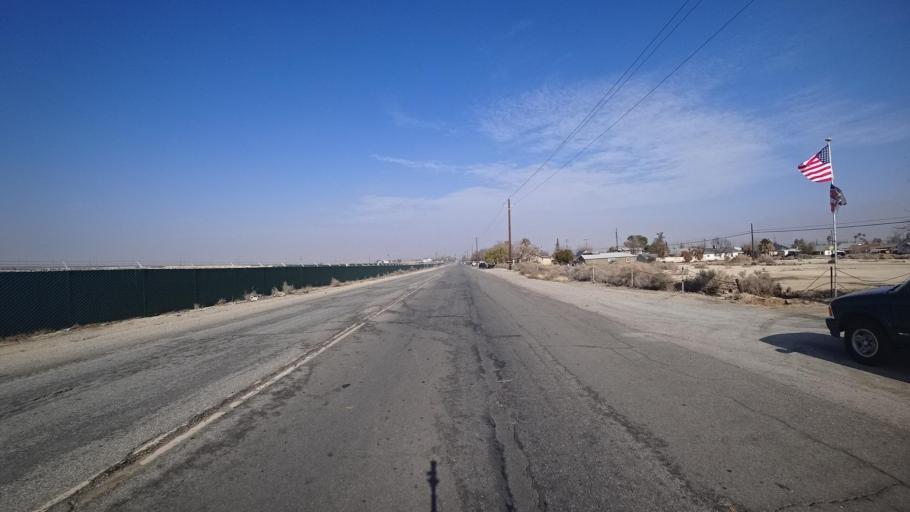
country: US
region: California
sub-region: Kern County
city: Ford City
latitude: 35.1613
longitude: -119.4652
